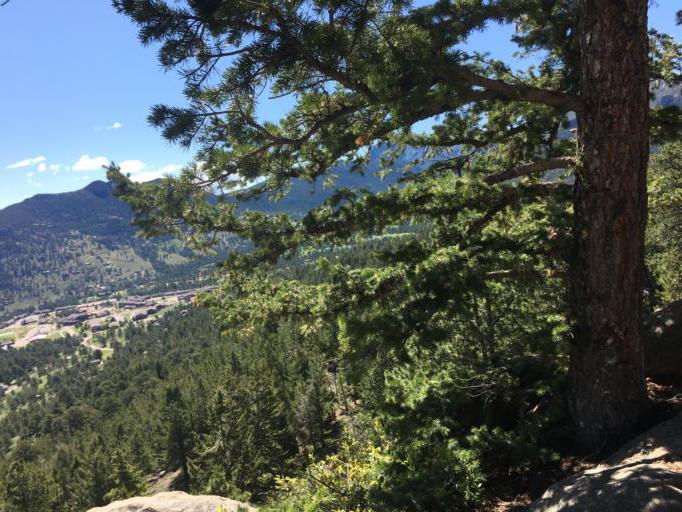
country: US
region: Colorado
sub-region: Larimer County
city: Estes Park
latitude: 40.3413
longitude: -105.5890
